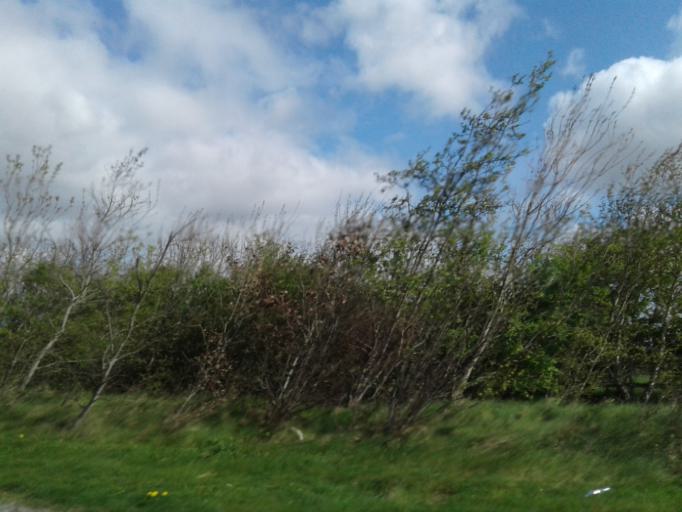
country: IE
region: Leinster
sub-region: An Mhi
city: Ashbourne
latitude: 53.4838
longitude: -6.3771
